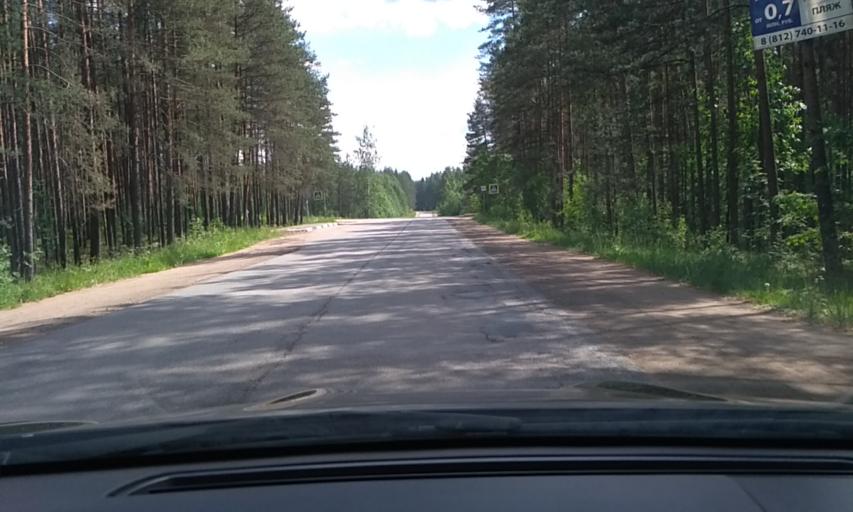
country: RU
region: Leningrad
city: Imeni Sverdlova
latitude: 59.8457
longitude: 30.6864
